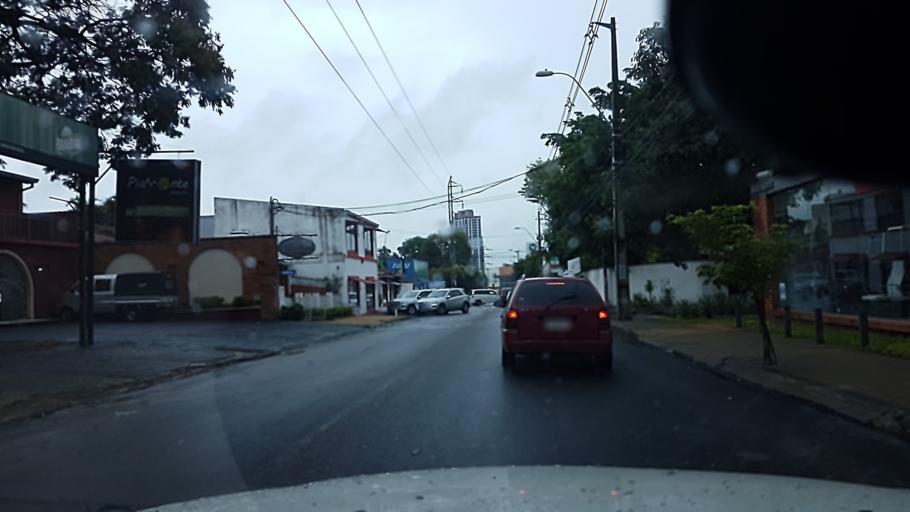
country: PY
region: Central
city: Fernando de la Mora
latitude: -25.2944
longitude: -57.5612
